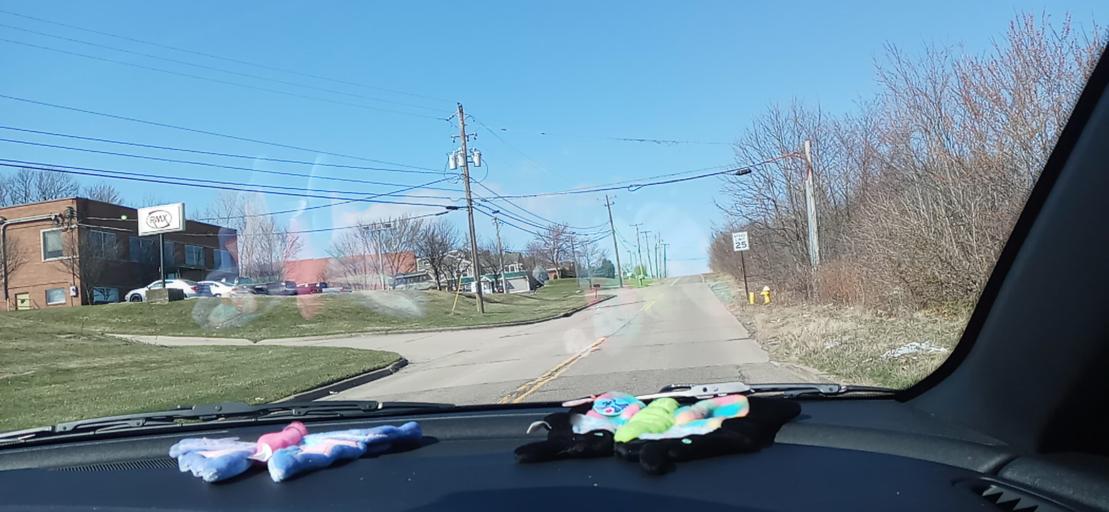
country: US
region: Ohio
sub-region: Summit County
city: Sawyerwood
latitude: 41.0294
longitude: -81.4827
